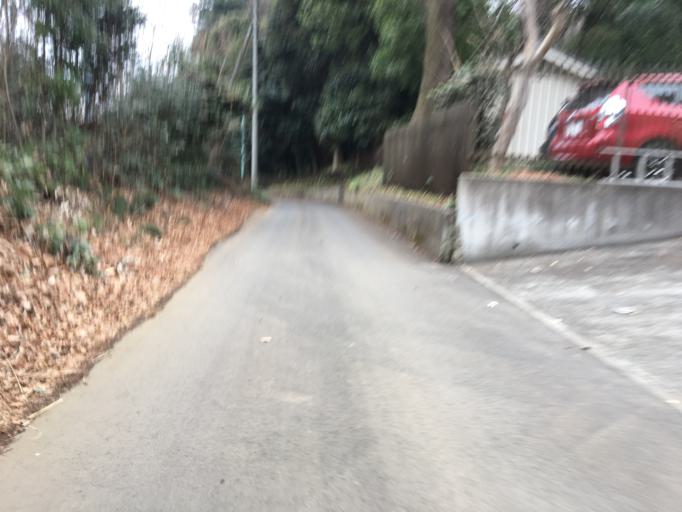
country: JP
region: Saitama
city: Oi
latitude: 35.8142
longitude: 139.5426
